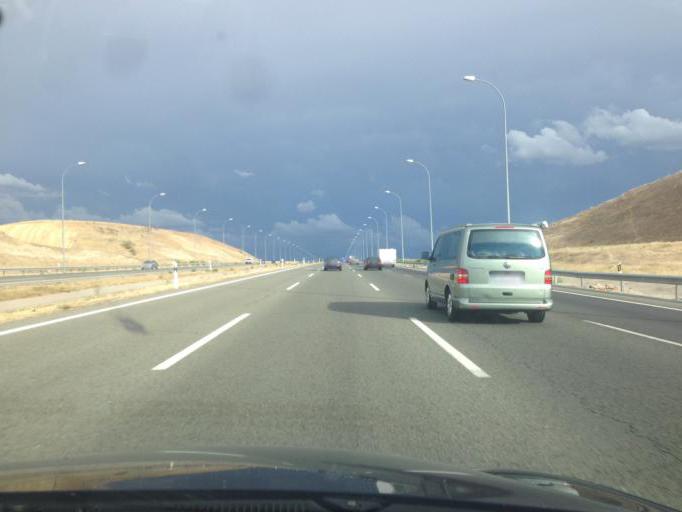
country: ES
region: Madrid
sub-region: Provincia de Madrid
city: Paracuellos de Jarama
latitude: 40.5349
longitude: -3.5247
